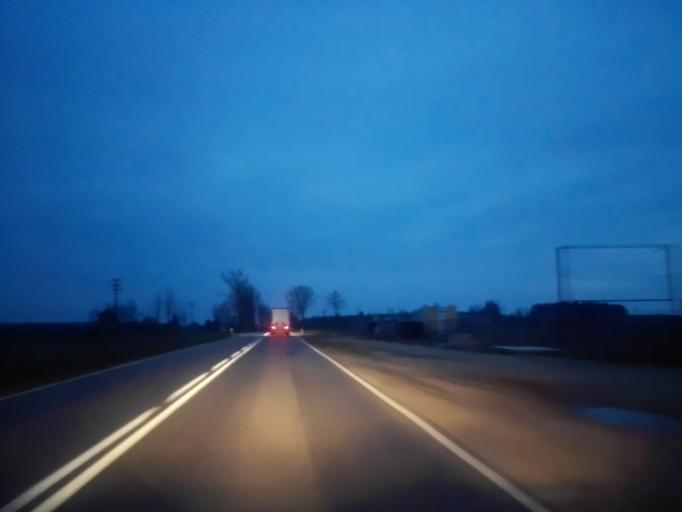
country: PL
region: Podlasie
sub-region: Lomza
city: Lomza
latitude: 53.1129
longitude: 22.0300
